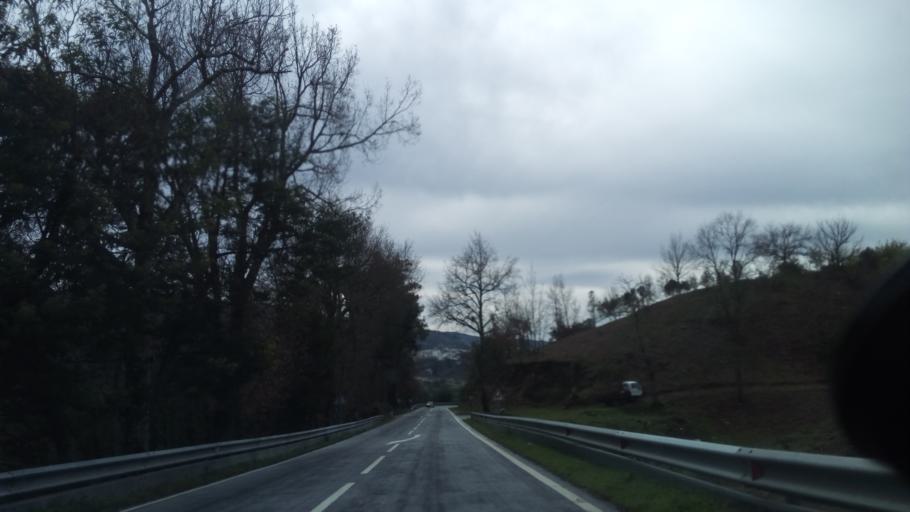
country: PT
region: Guarda
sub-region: Seia
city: Seia
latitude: 40.4410
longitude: -7.7092
